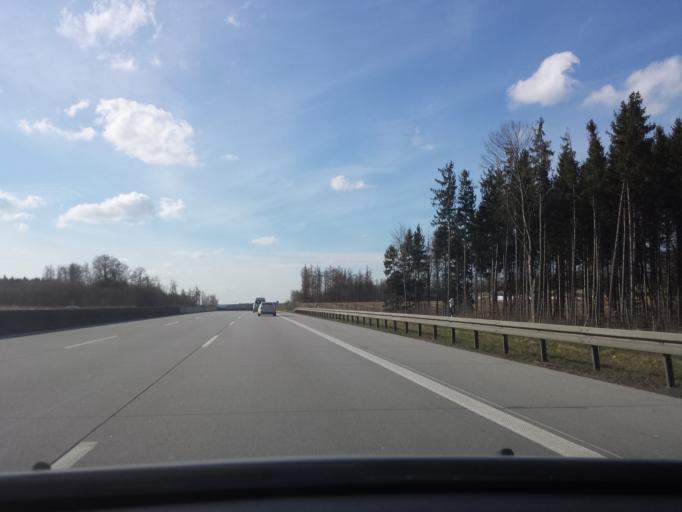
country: DE
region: Bavaria
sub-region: Upper Bavaria
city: Sulzemoos
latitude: 48.2778
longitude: 11.2765
